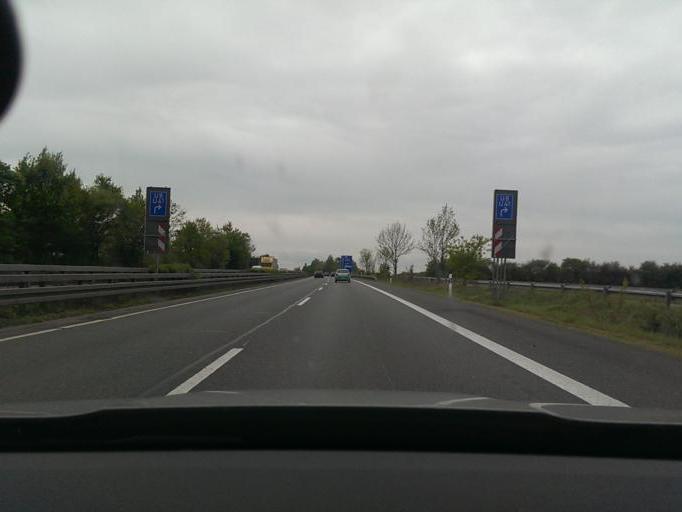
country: DE
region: Lower Saxony
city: Wolfsburg
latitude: 52.3783
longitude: 10.7260
